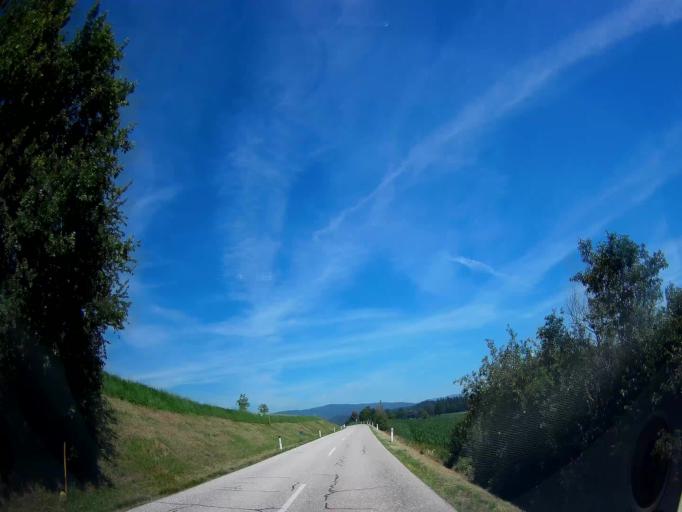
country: AT
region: Carinthia
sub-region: Politischer Bezirk Sankt Veit an der Glan
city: St. Georgen am Laengsee
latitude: 46.7922
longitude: 14.4181
